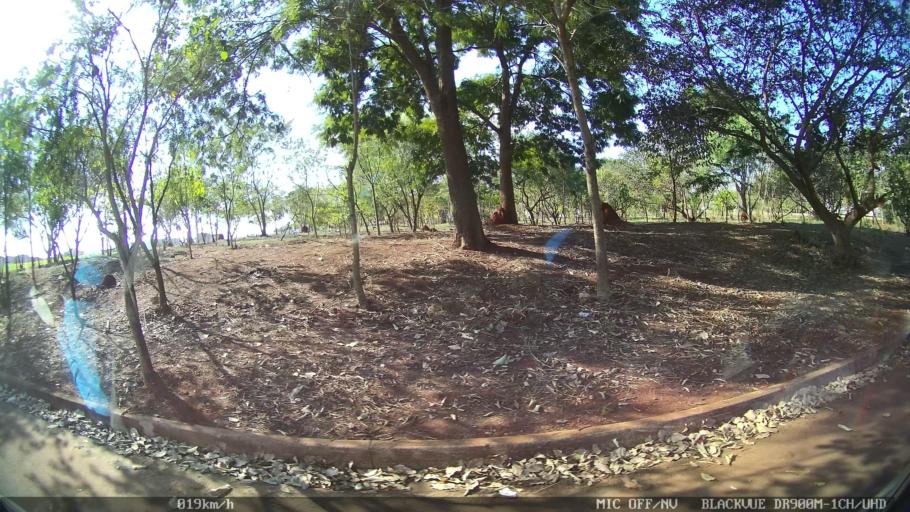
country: BR
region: Sao Paulo
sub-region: Sumare
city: Sumare
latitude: -22.8243
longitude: -47.2930
